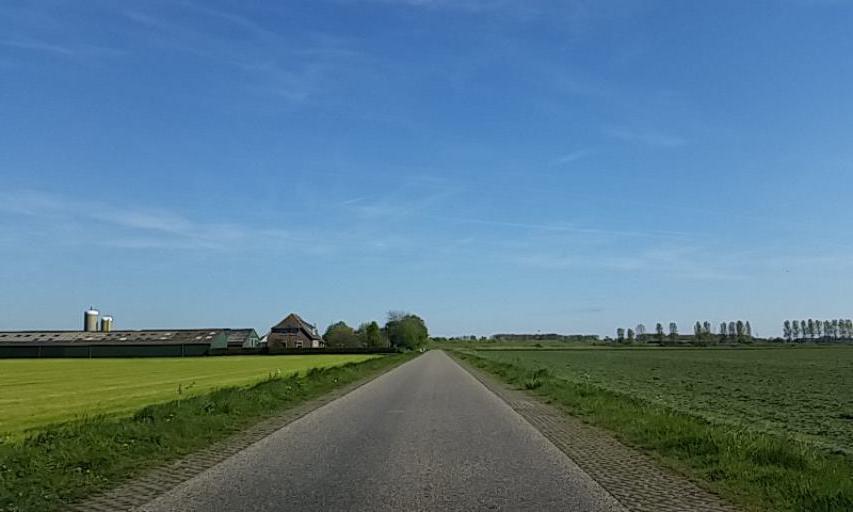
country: NL
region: Zeeland
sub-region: Gemeente Borsele
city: Borssele
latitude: 51.3337
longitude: 3.7142
